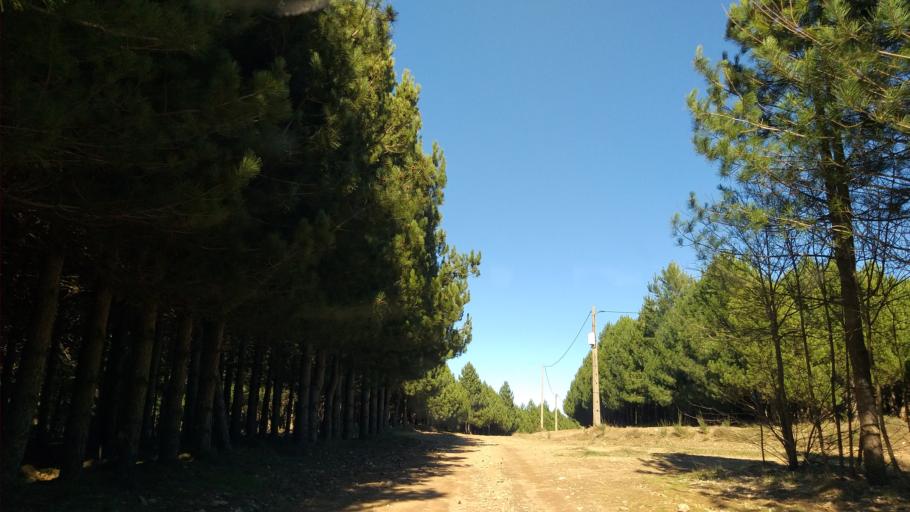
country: PT
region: Guarda
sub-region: Manteigas
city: Manteigas
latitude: 40.5100
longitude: -7.4605
